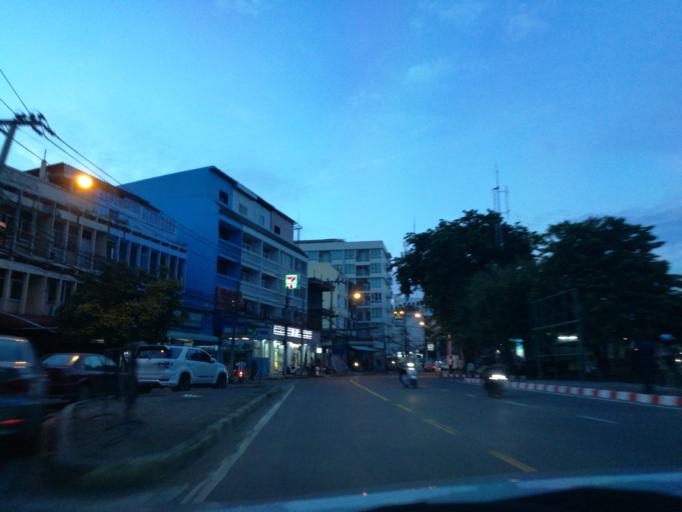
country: TH
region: Bangkok
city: Dusit
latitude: 13.7789
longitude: 100.5296
